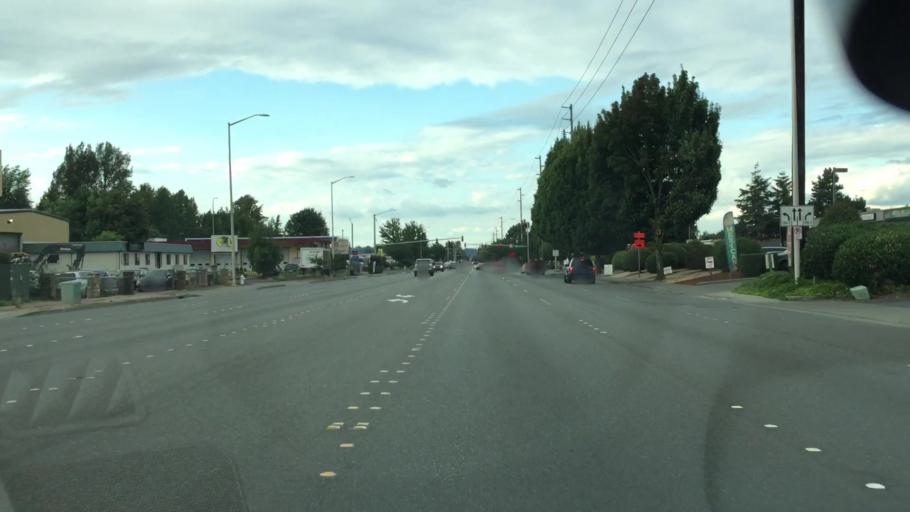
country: US
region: Washington
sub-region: King County
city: Kent
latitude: 47.4102
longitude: -122.2280
